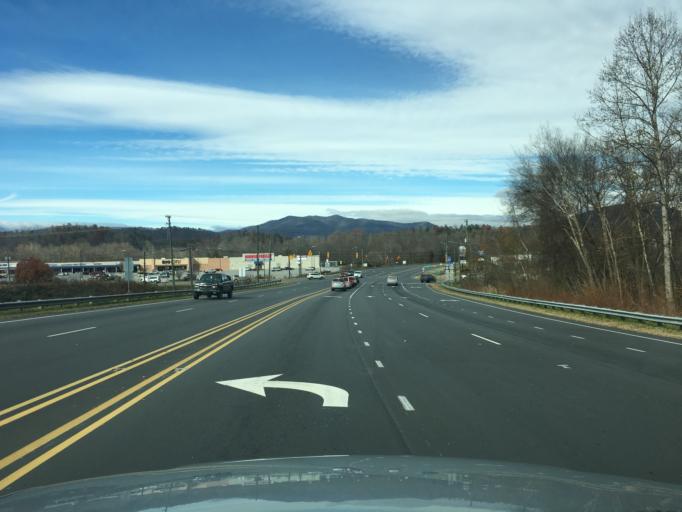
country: US
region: North Carolina
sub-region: McDowell County
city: Marion
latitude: 35.7030
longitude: -82.0353
